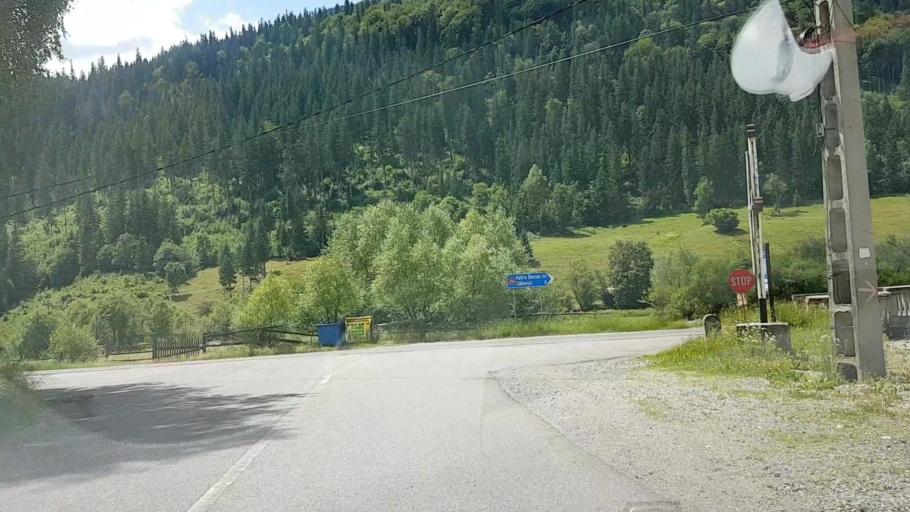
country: RO
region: Suceava
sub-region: Comuna Crucea
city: Crucea
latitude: 47.3964
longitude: 25.5637
